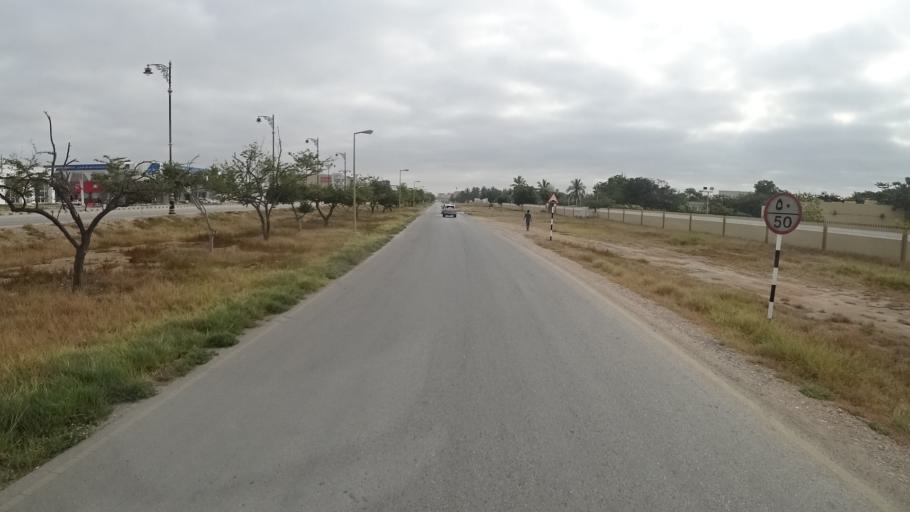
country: OM
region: Zufar
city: Salalah
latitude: 17.0108
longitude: 54.0468
